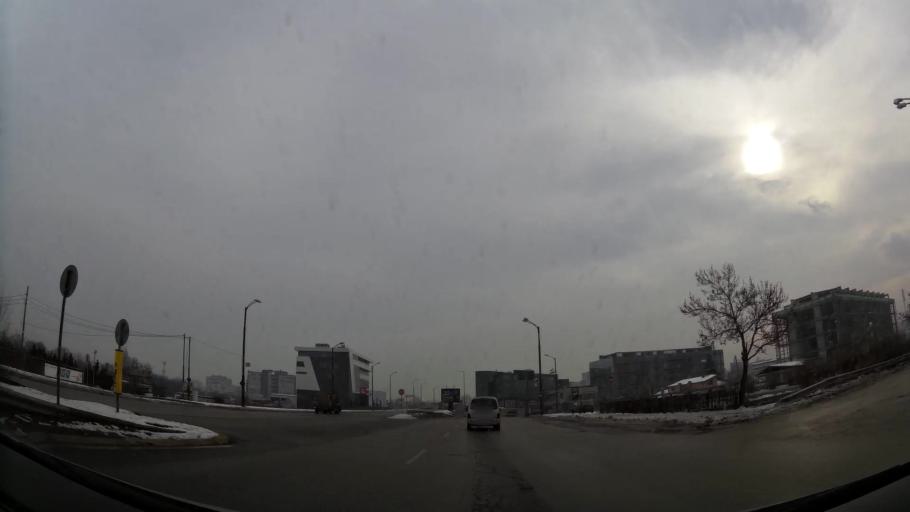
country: BG
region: Sofia-Capital
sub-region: Stolichna Obshtina
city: Sofia
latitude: 42.7104
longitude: 23.3636
